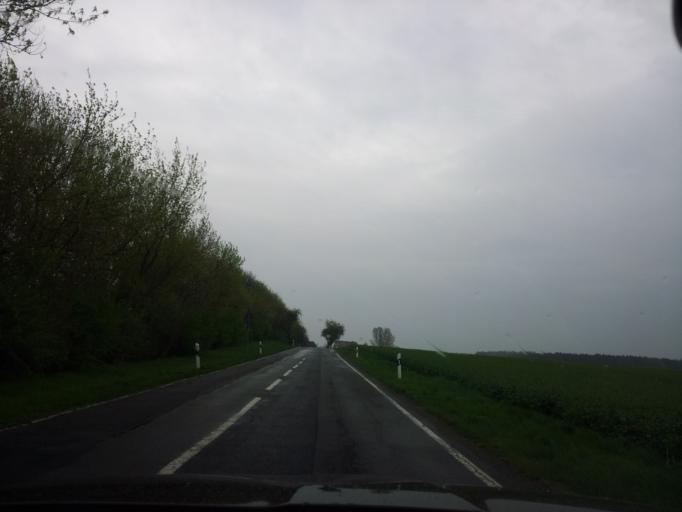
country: DE
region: Saxony-Anhalt
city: Zahna
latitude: 51.9799
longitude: 12.8243
